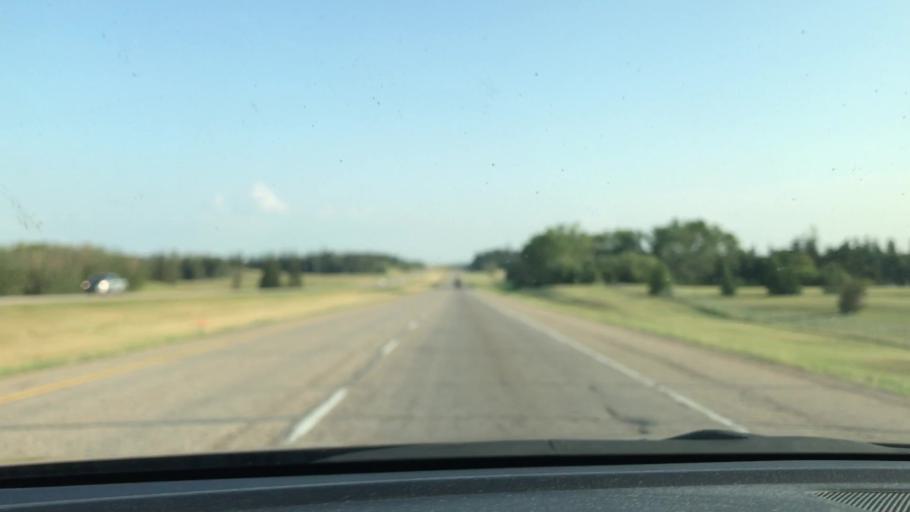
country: CA
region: Alberta
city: Ponoka
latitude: 52.6040
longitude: -113.6636
